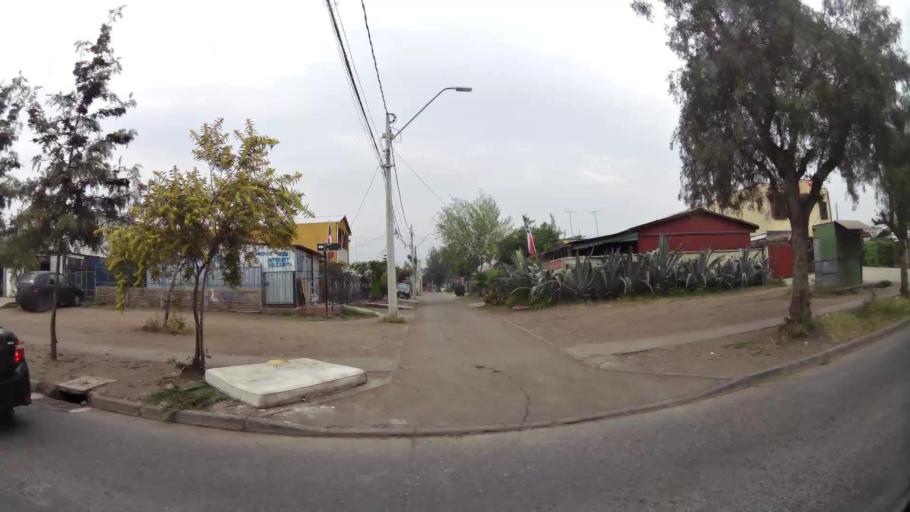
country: CL
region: Santiago Metropolitan
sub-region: Provincia de Chacabuco
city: Chicureo Abajo
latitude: -33.1970
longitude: -70.6752
